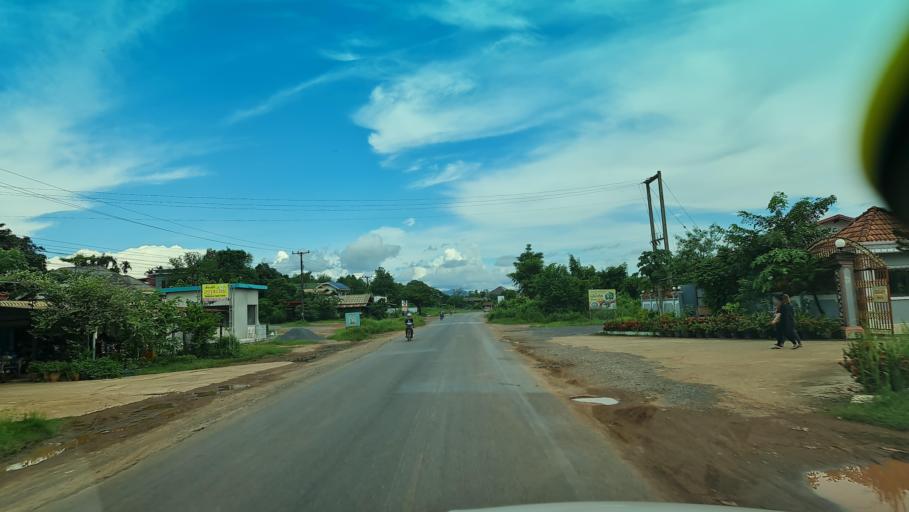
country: LA
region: Bolikhamxai
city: Ban Nahin
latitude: 18.1101
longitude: 104.2774
